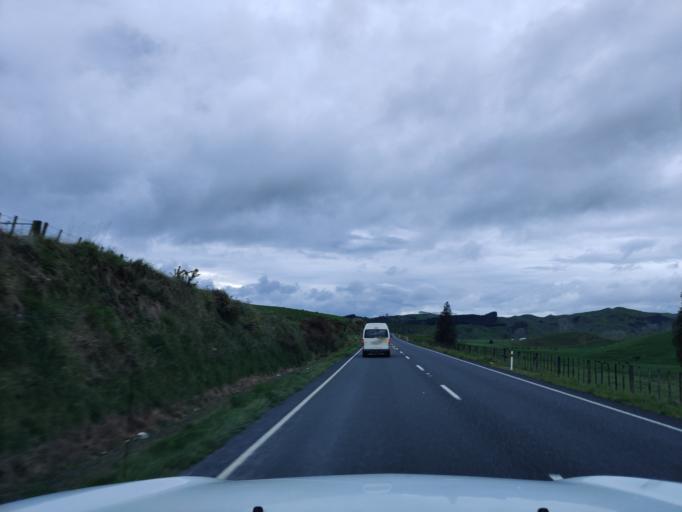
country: NZ
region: Waikato
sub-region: Otorohanga District
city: Otorohanga
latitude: -38.4624
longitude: 175.1679
